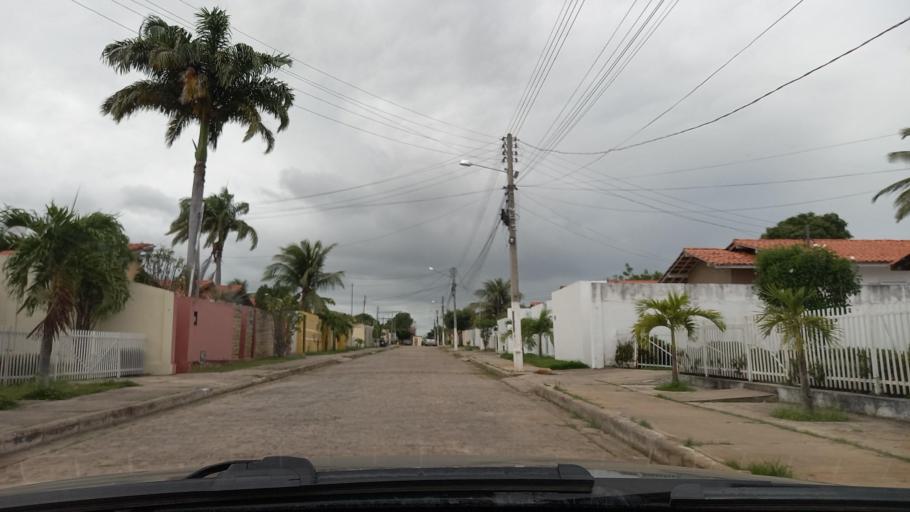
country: BR
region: Sergipe
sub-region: Caninde De Sao Francisco
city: Caninde de Sao Francisco
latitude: -9.6158
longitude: -37.7669
